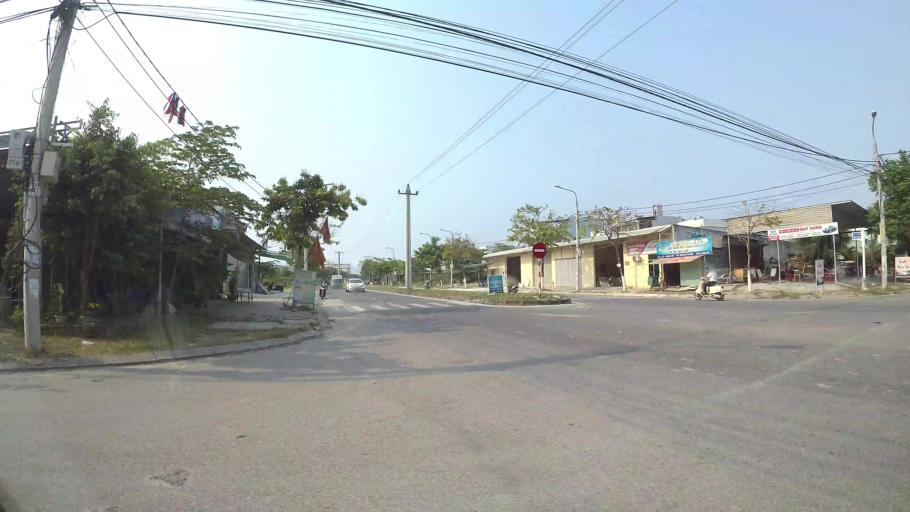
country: VN
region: Da Nang
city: Thanh Khe
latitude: 16.0457
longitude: 108.1755
